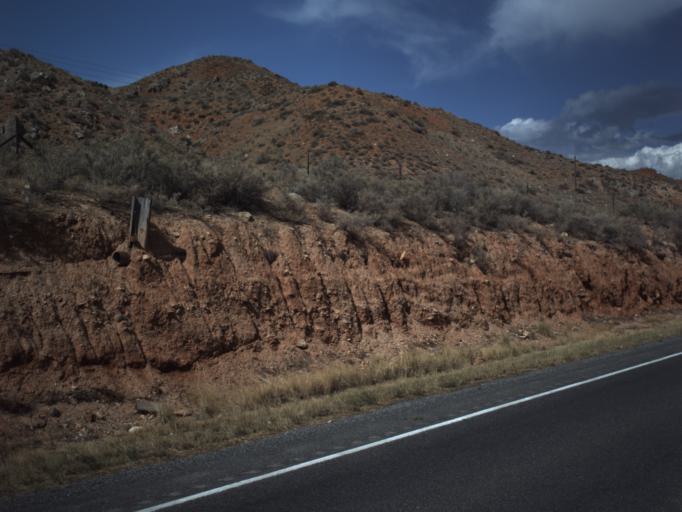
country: US
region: Utah
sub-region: Sanpete County
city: Gunnison
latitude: 39.1609
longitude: -111.7459
